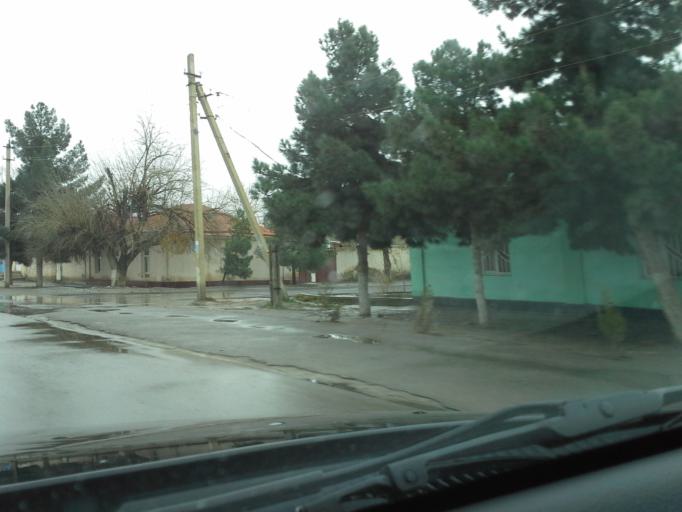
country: TM
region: Ahal
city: Ashgabat
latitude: 37.9514
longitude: 58.4202
